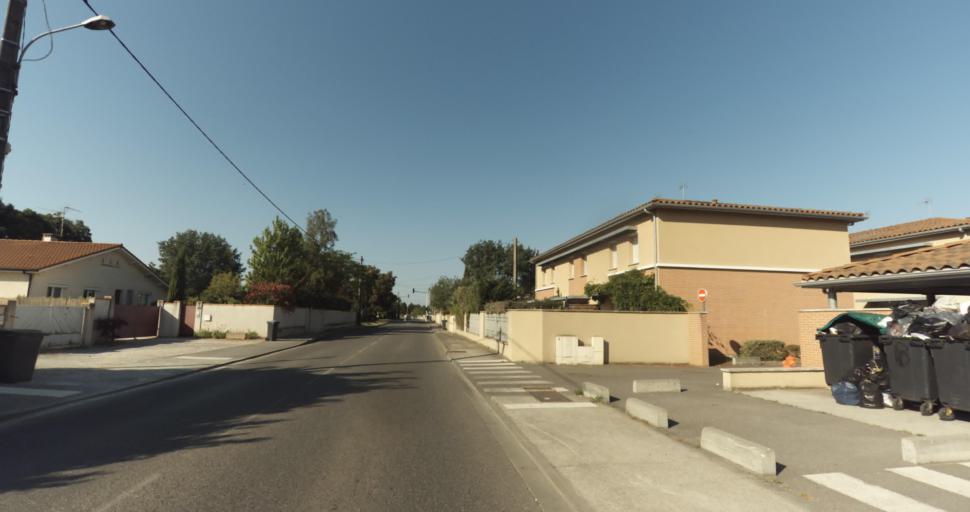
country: FR
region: Midi-Pyrenees
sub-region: Departement de la Haute-Garonne
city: La Salvetat-Saint-Gilles
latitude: 43.5742
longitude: 1.2711
